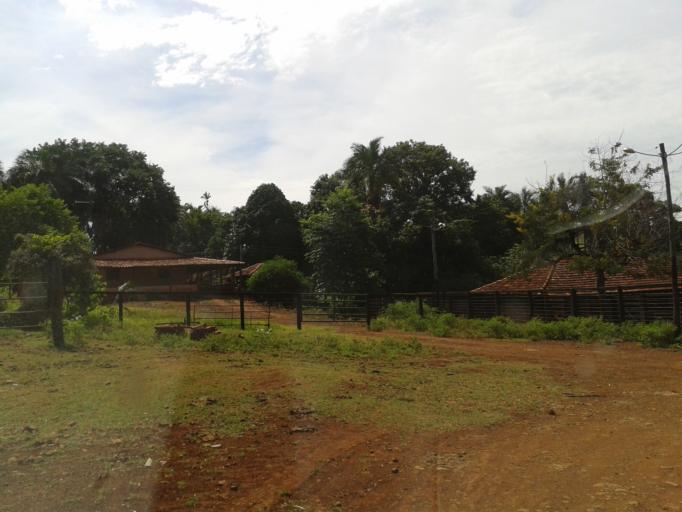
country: BR
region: Minas Gerais
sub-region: Centralina
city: Centralina
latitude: -18.6924
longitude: -49.2092
